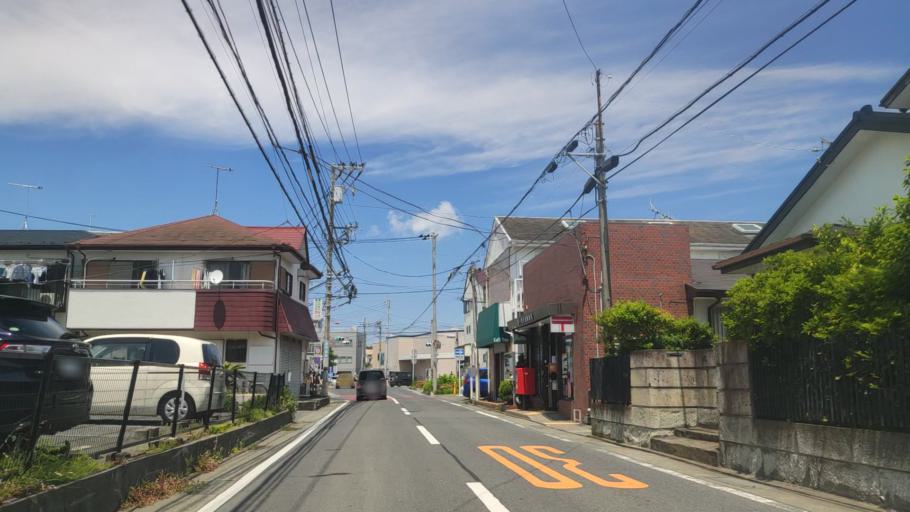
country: JP
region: Kanagawa
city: Chigasaki
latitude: 35.3420
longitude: 139.3980
